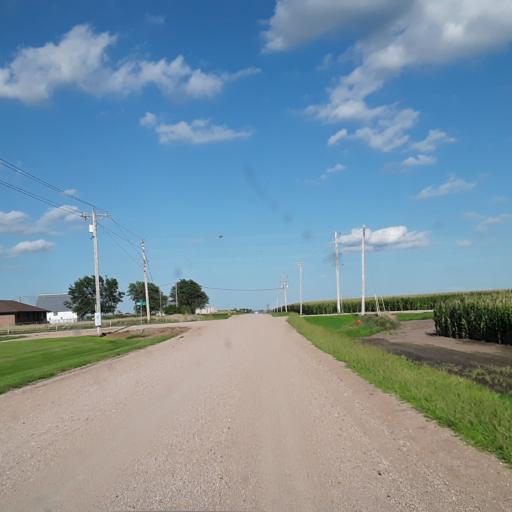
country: US
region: Nebraska
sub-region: Hall County
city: Wood River
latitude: 40.9168
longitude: -98.5898
